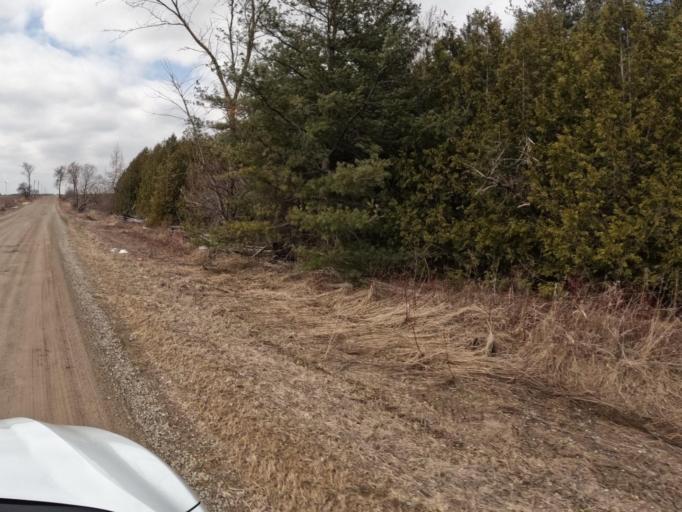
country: CA
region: Ontario
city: Shelburne
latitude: 44.0499
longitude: -80.2940
